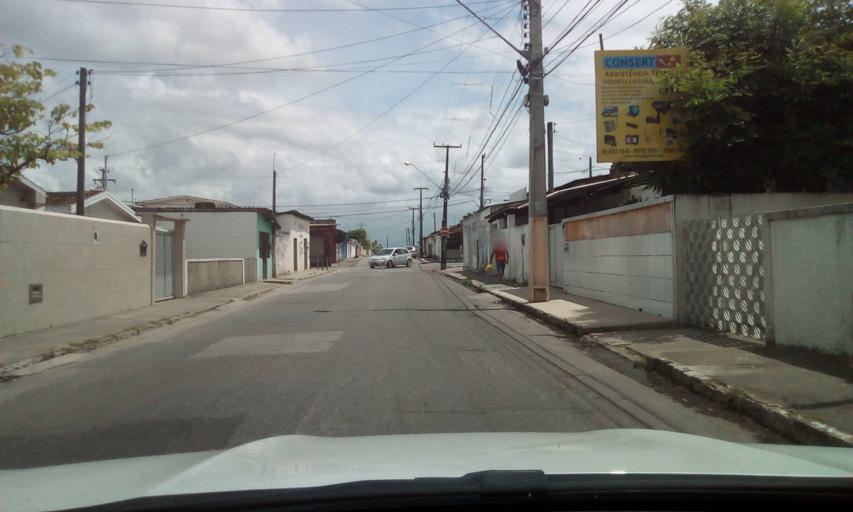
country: BR
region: Paraiba
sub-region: Bayeux
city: Bayeux
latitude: -7.1798
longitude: -34.8958
